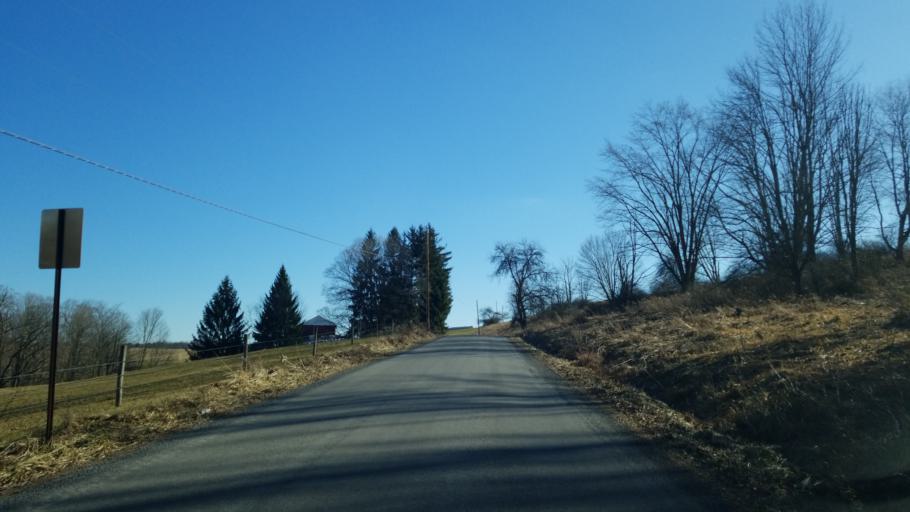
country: US
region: Pennsylvania
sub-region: Jefferson County
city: Sykesville
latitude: 41.0450
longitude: -78.7858
